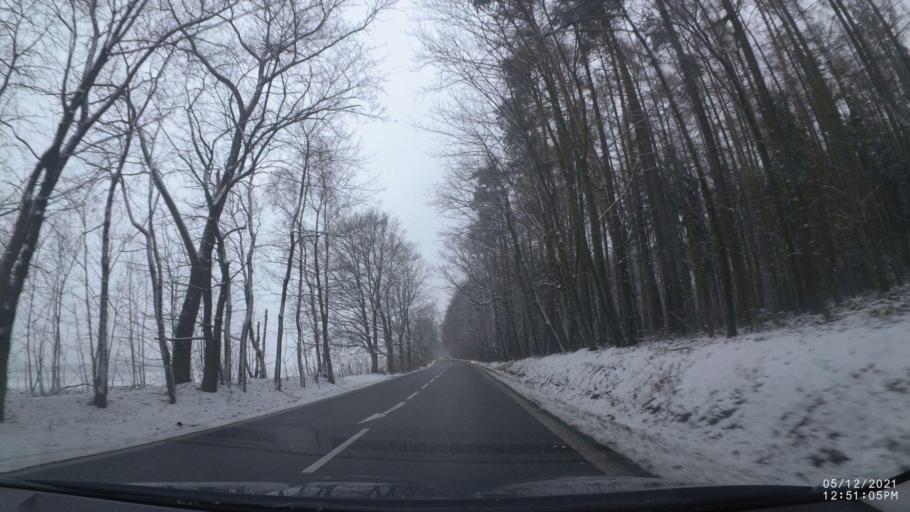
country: CZ
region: Kralovehradecky
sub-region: Okres Nachod
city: Nachod
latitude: 50.3931
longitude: 16.1402
